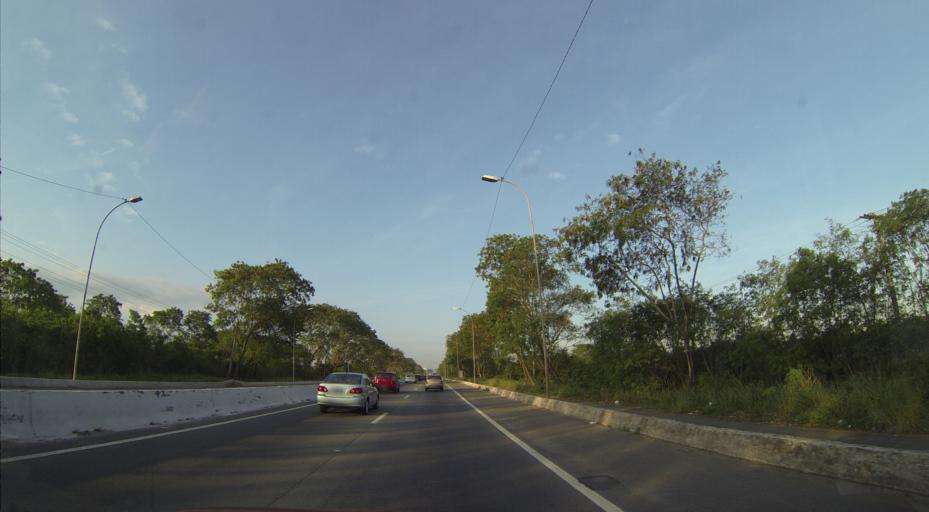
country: BR
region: Espirito Santo
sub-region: Vila Velha
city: Vila Velha
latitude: -20.2520
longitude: -40.2873
